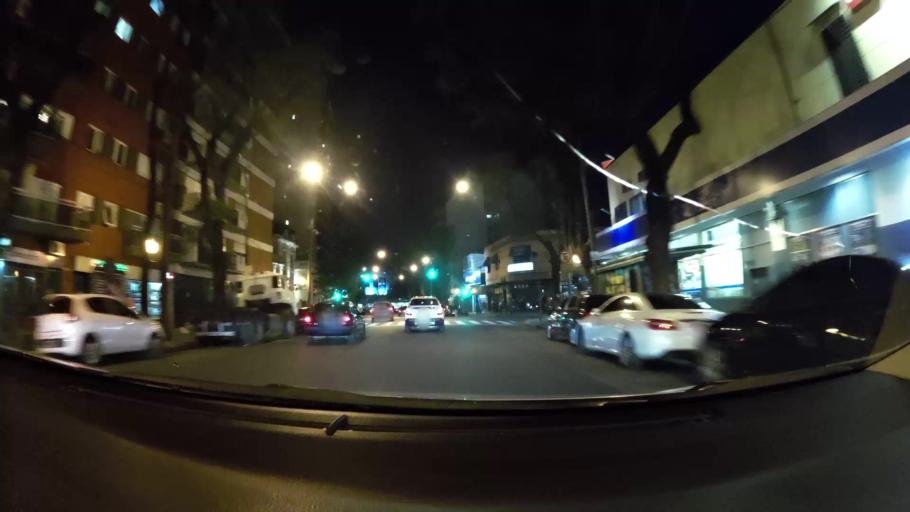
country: AR
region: Buenos Aires F.D.
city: Colegiales
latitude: -34.5712
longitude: -58.4583
